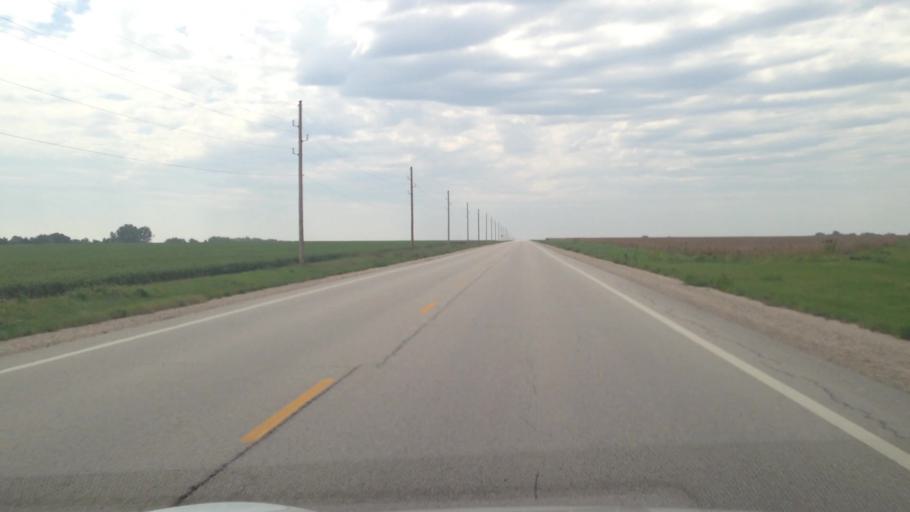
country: US
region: Kansas
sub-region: Anderson County
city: Garnett
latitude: 38.0624
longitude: -95.1694
